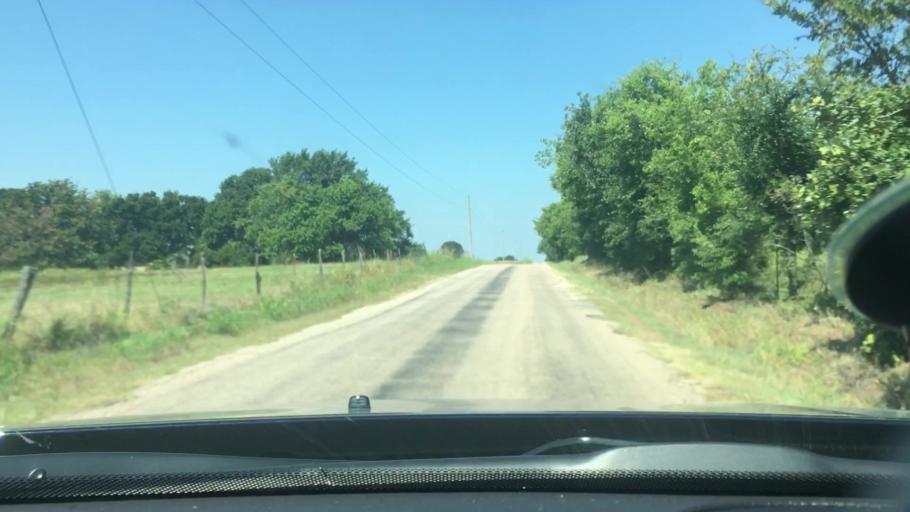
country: US
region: Oklahoma
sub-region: Johnston County
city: Tishomingo
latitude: 34.3176
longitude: -96.6554
